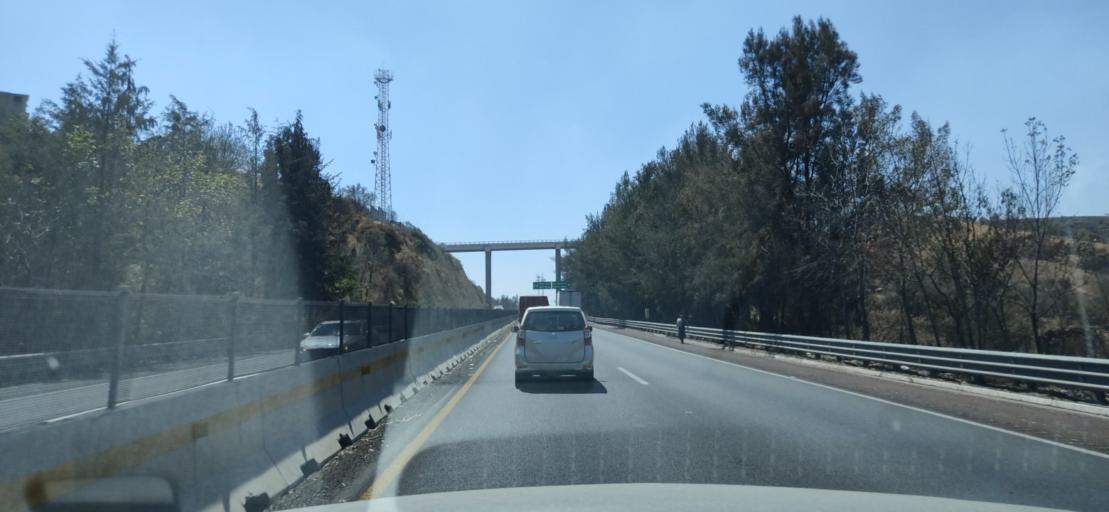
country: MX
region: Mexico
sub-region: Naucalpan de Juarez
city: Rincon Verde
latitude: 19.4965
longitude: -99.3080
